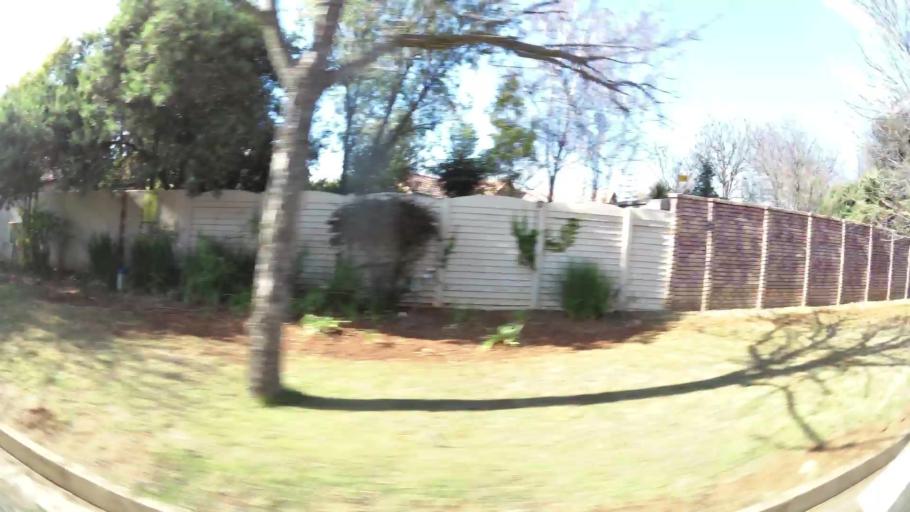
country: ZA
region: Gauteng
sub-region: Ekurhuleni Metropolitan Municipality
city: Benoni
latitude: -26.1447
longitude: 28.3363
